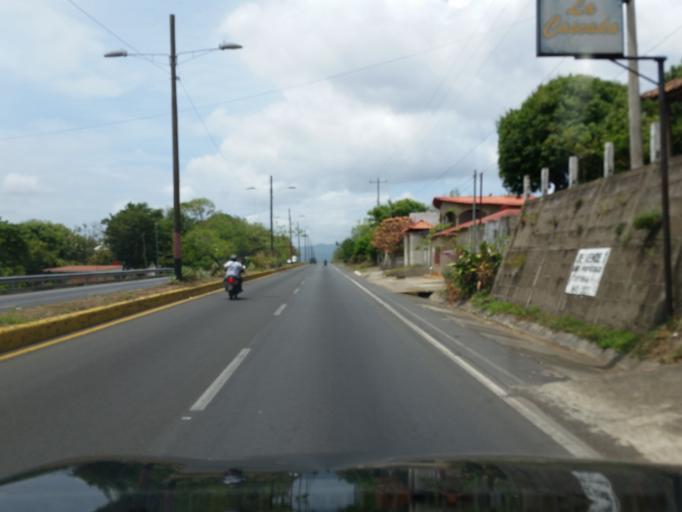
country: NI
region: Masaya
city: Nindiri
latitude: 12.0097
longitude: -86.1390
